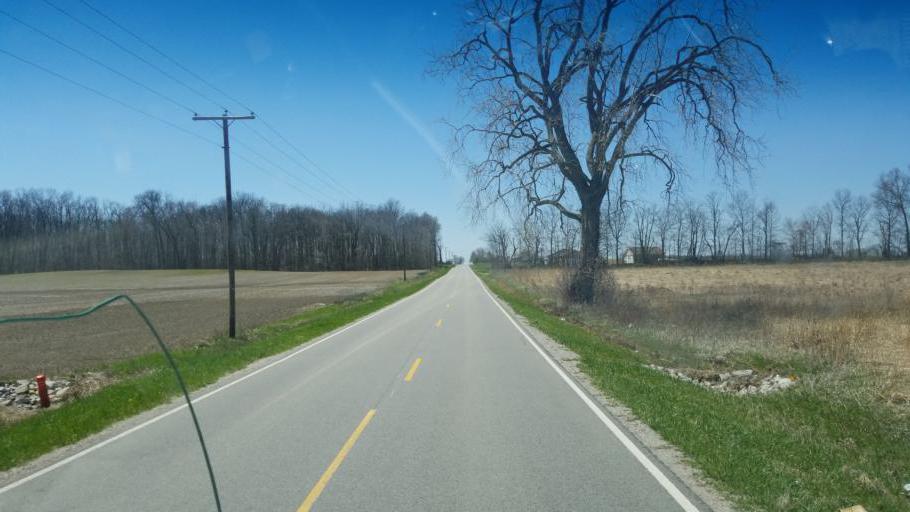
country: US
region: Ohio
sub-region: Huron County
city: Willard
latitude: 41.0683
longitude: -82.6732
